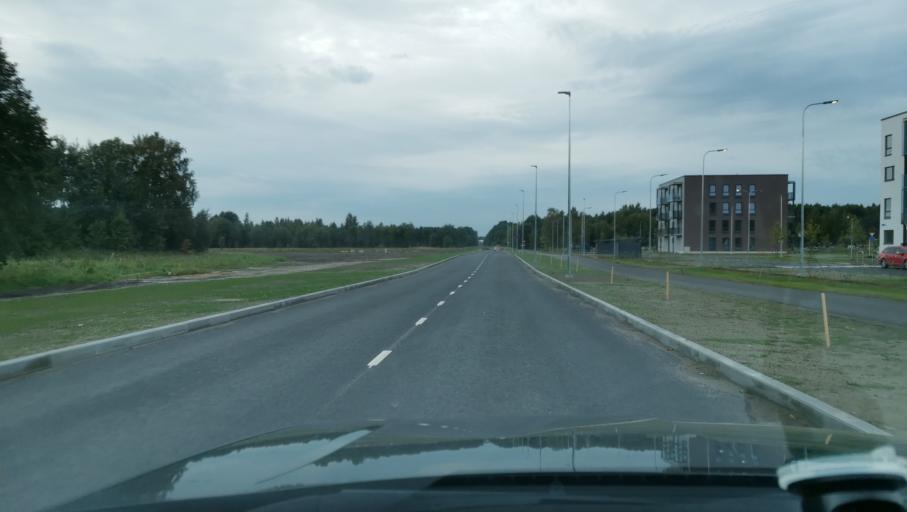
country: EE
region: Harju
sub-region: Saue vald
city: Laagri
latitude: 59.4182
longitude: 24.6315
